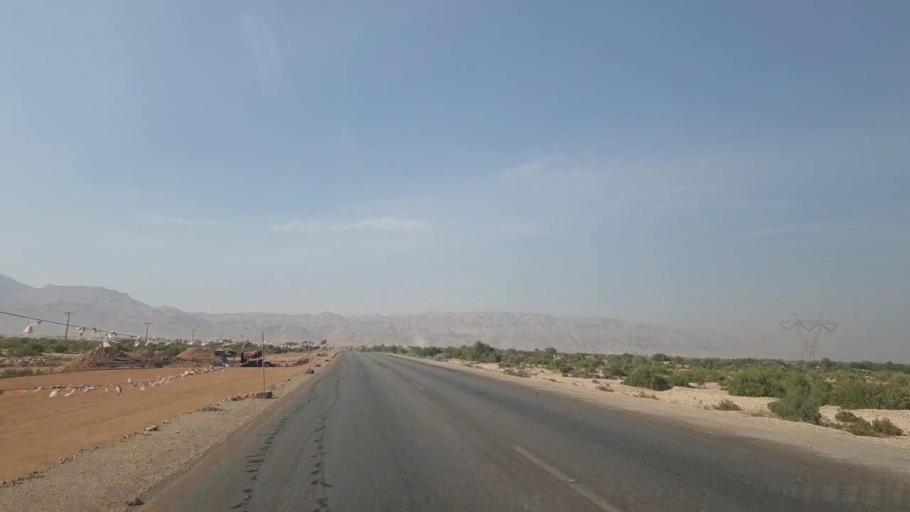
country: PK
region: Sindh
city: Sehwan
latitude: 26.2149
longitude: 67.9170
